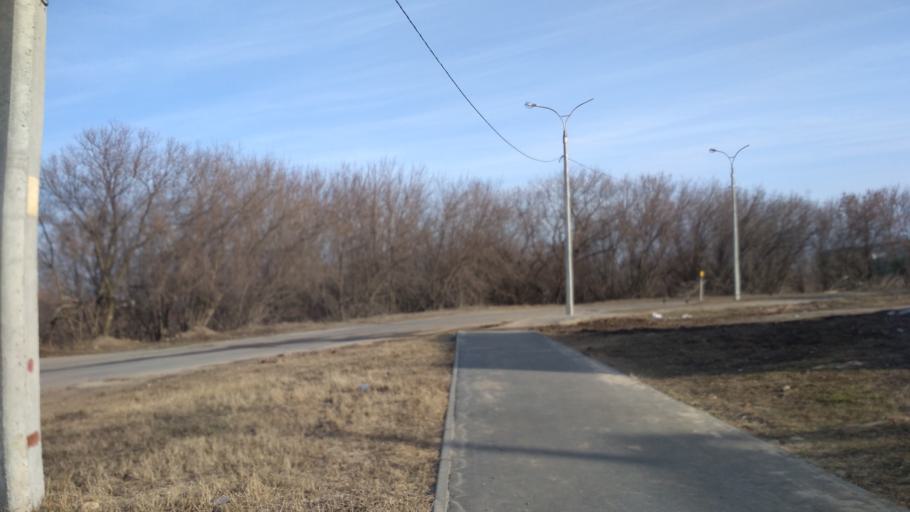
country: RU
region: Chuvashia
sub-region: Cheboksarskiy Rayon
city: Cheboksary
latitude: 56.1352
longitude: 47.3157
